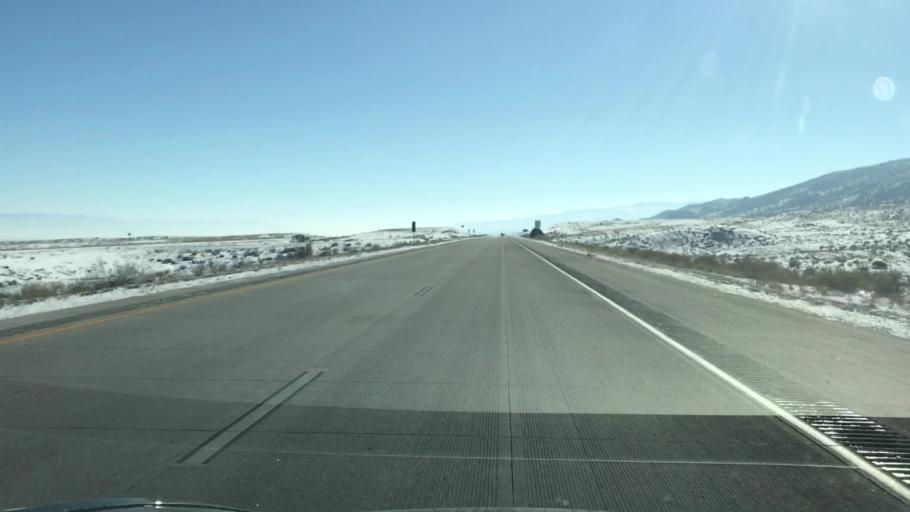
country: US
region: Colorado
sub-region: Mesa County
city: Loma
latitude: 39.2075
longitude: -108.8608
